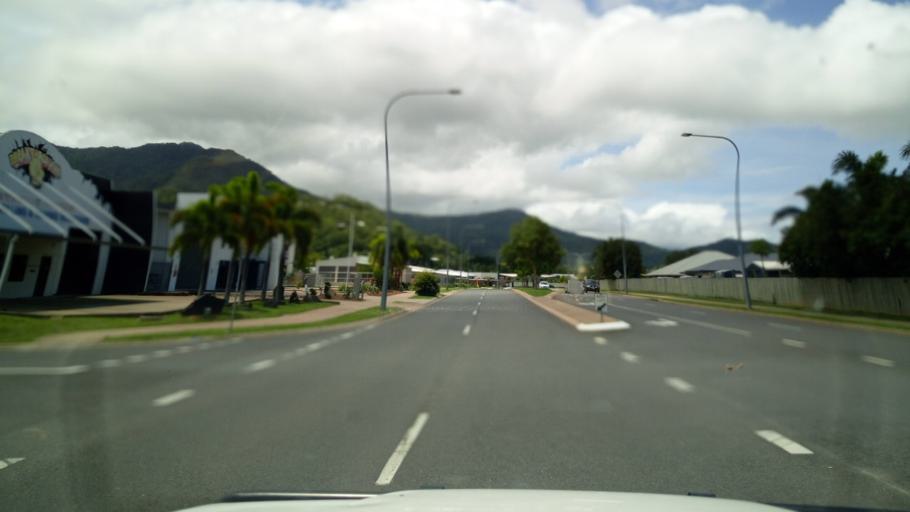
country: AU
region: Queensland
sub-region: Cairns
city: Yorkeys Knob
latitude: -16.8338
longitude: 145.6961
